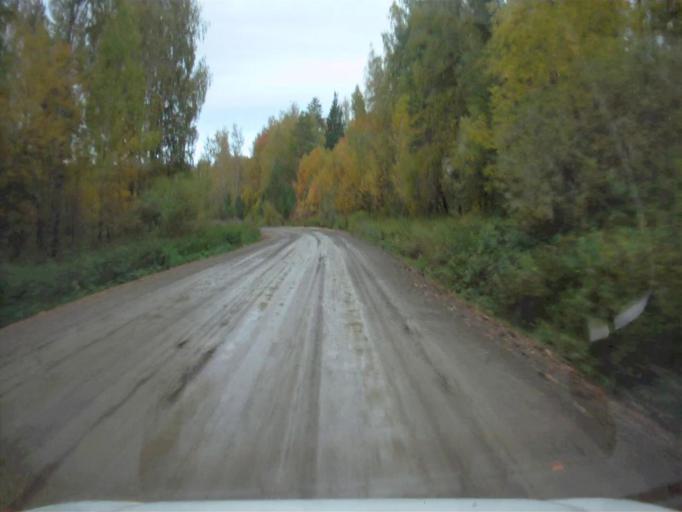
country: RU
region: Chelyabinsk
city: Nyazepetrovsk
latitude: 56.1196
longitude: 59.3696
